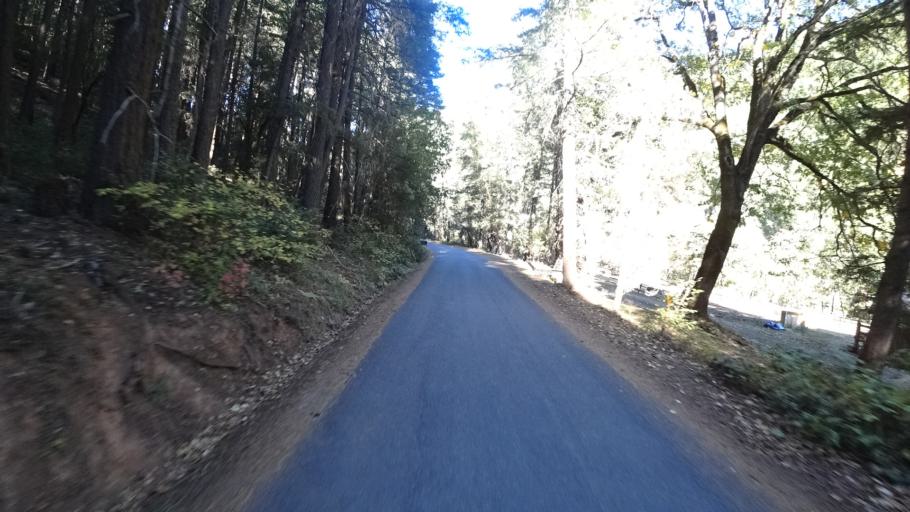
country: US
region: California
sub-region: Siskiyou County
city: Happy Camp
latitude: 41.3172
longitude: -123.1793
